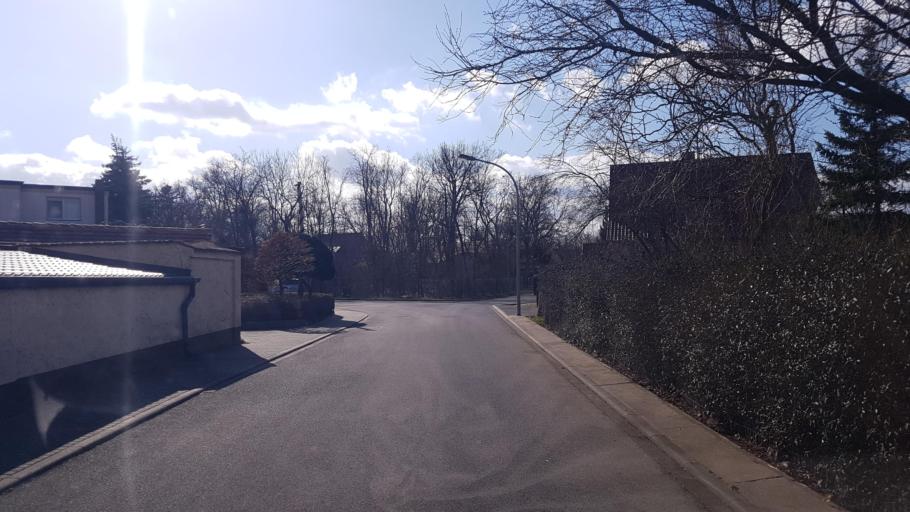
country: DE
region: Brandenburg
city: Herzberg
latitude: 51.6981
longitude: 13.2296
